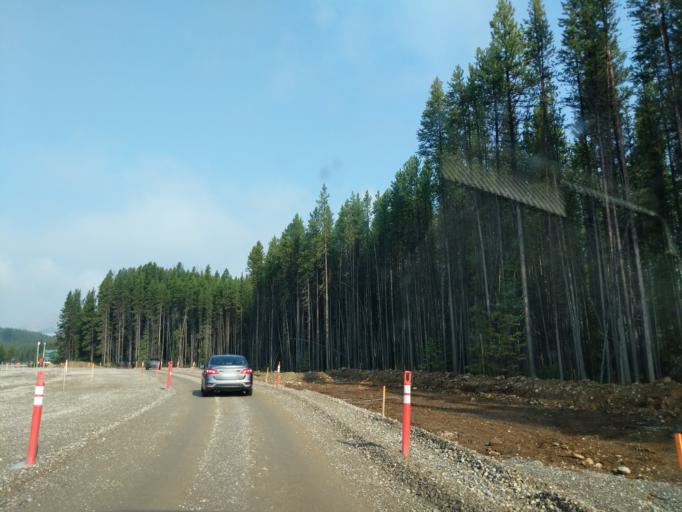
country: CA
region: Alberta
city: Lake Louise
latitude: 51.4448
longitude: -116.2082
